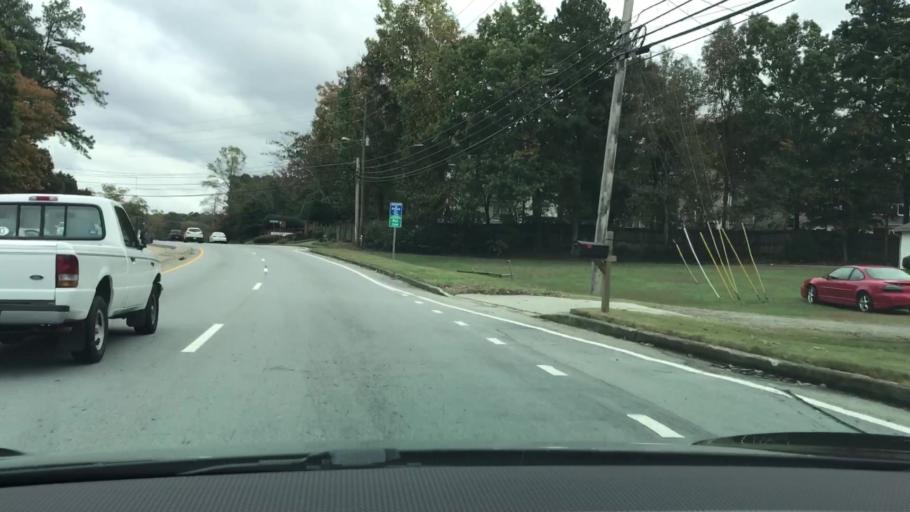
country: US
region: Georgia
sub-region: Gwinnett County
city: Lawrenceville
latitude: 33.9913
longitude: -84.0325
